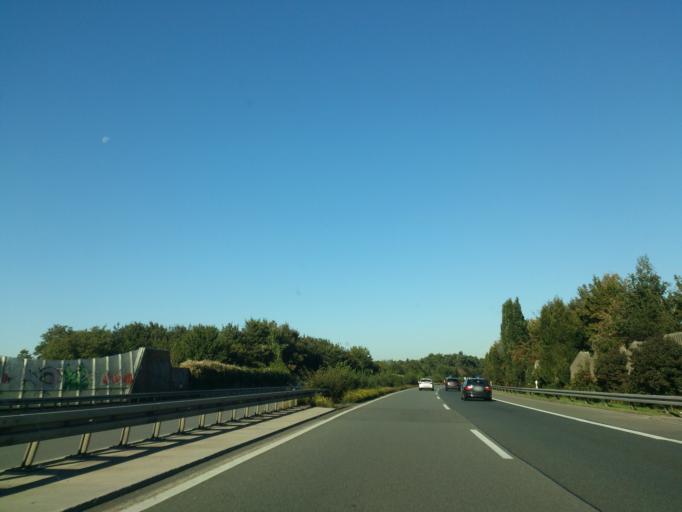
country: DE
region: North Rhine-Westphalia
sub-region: Regierungsbezirk Detmold
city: Oerlinghausen
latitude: 51.9255
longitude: 8.5871
